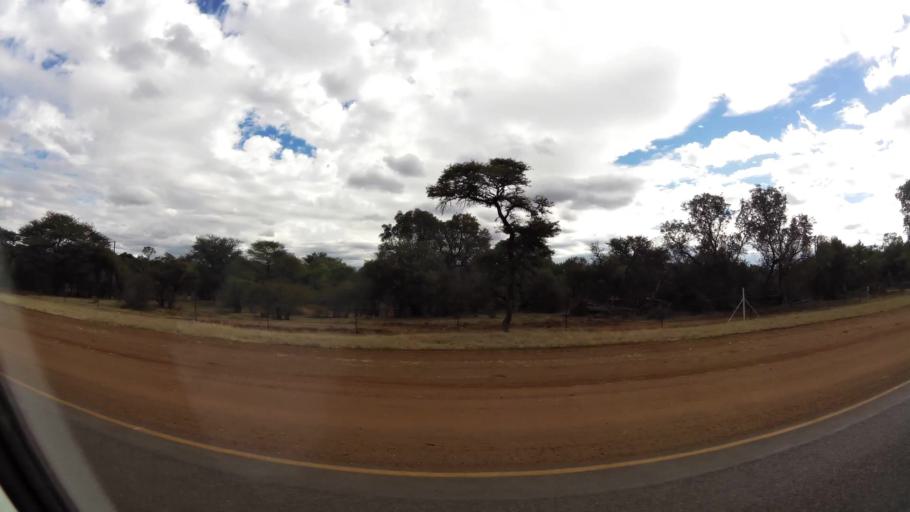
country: ZA
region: Limpopo
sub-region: Waterberg District Municipality
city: Warmbaths
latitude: -24.9009
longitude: 28.2796
